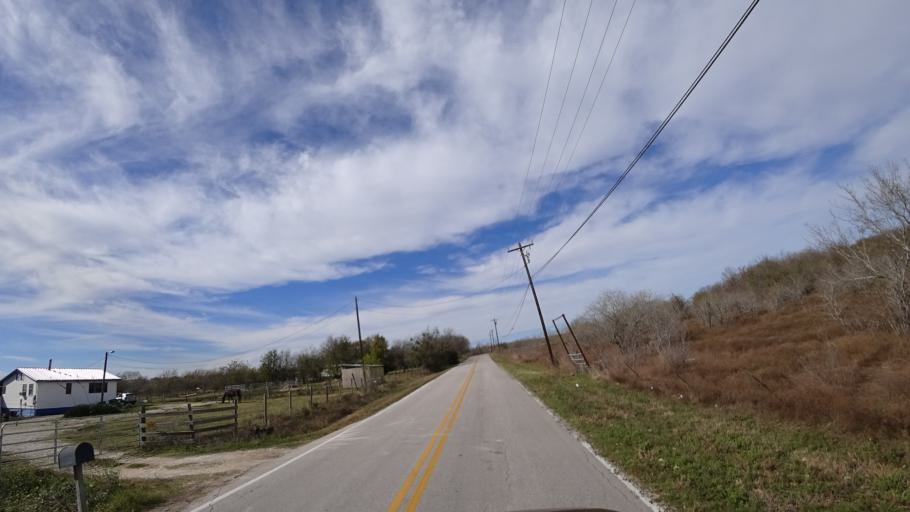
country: US
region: Texas
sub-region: Travis County
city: Onion Creek
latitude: 30.1202
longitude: -97.7132
